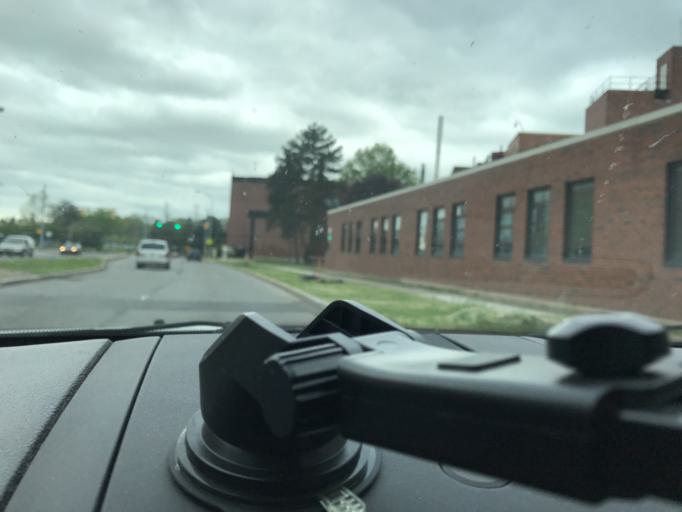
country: US
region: New York
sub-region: Monroe County
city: Rochester
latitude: 43.1240
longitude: -77.6267
